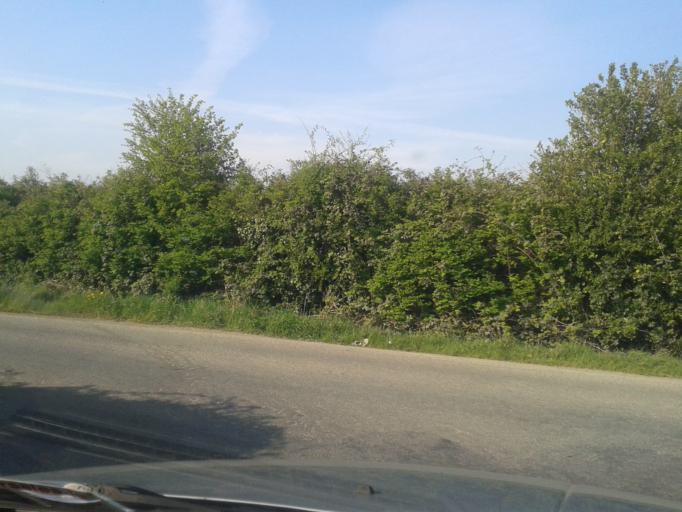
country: IE
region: Leinster
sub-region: Fingal County
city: Swords
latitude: 53.4777
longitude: -6.2233
